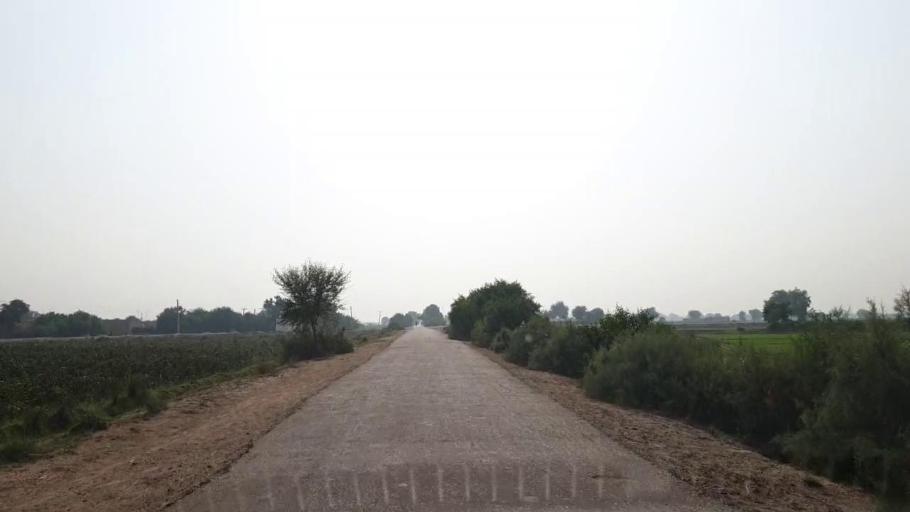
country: PK
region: Sindh
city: Bhan
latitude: 26.4802
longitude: 67.7705
